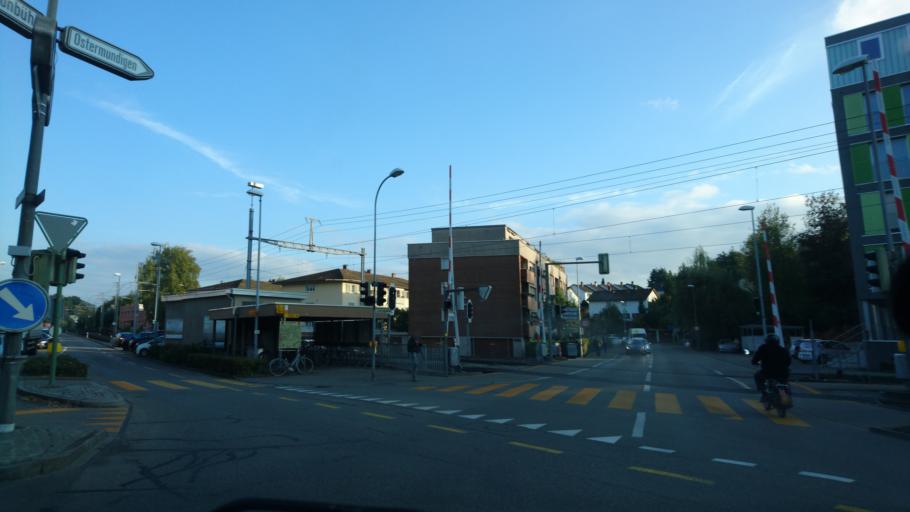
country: CH
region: Bern
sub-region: Bern-Mittelland District
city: Bolligen
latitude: 46.9735
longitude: 7.4845
